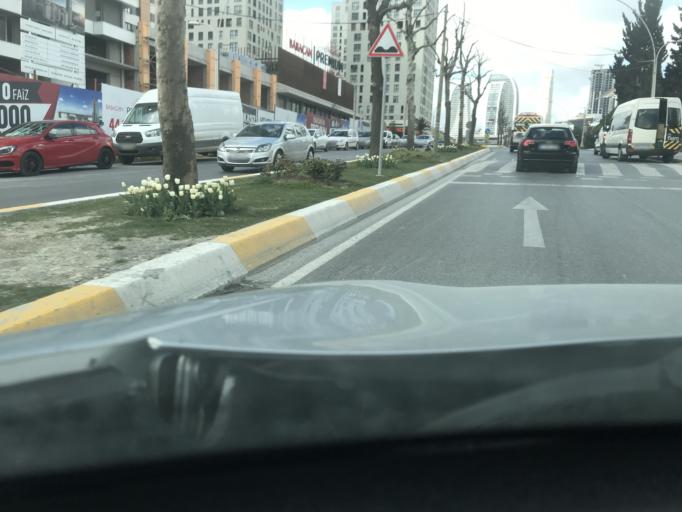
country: TR
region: Istanbul
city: Yakuplu
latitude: 41.0069
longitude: 28.6820
